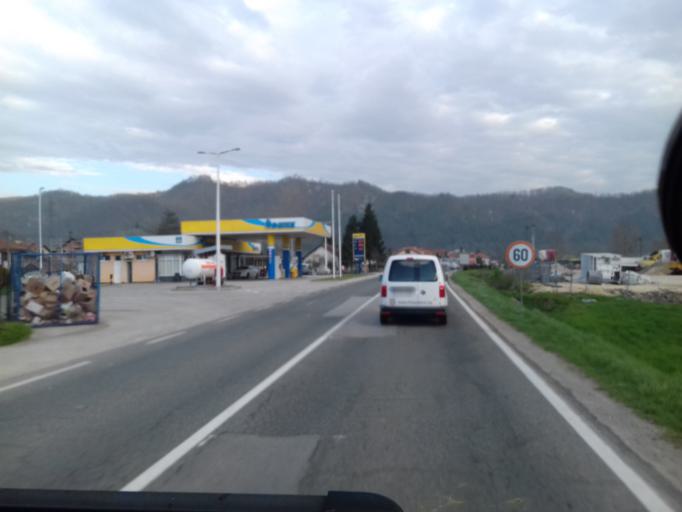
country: BA
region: Federation of Bosnia and Herzegovina
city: Maglaj
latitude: 44.5942
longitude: 18.0922
